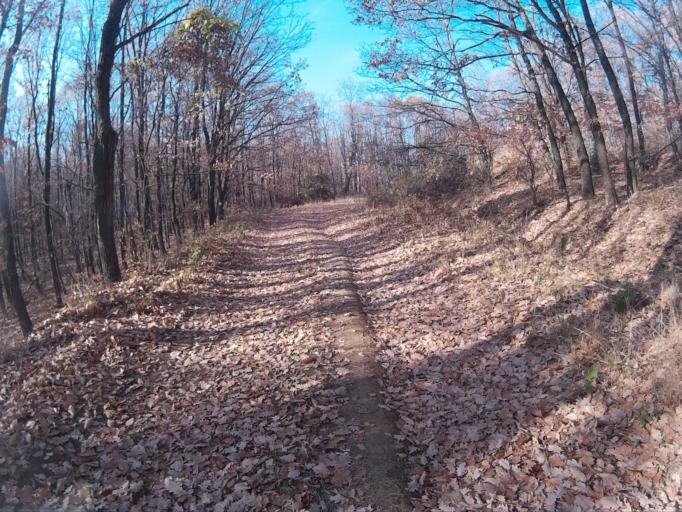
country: HU
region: Heves
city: Belapatfalva
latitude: 48.0247
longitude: 20.3942
